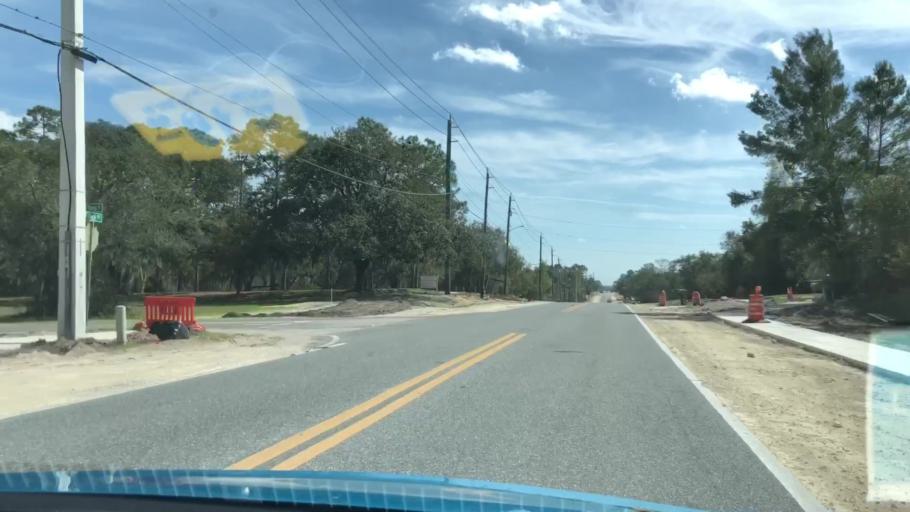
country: US
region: Florida
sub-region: Seminole County
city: Midway
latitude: 28.8589
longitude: -81.1949
